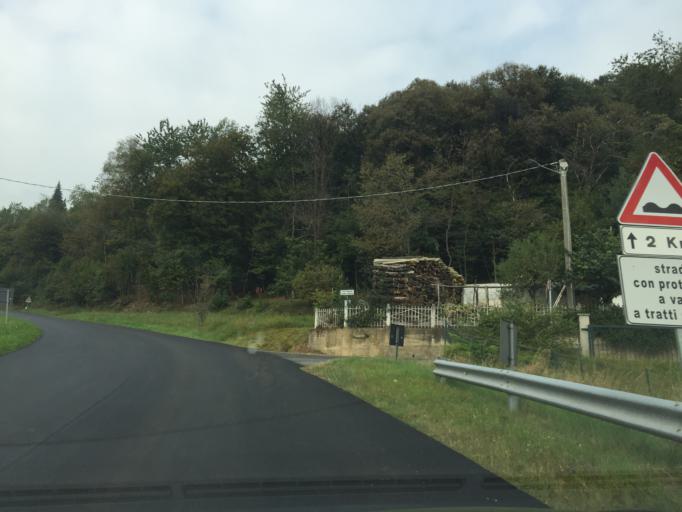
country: IT
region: Piedmont
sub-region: Provincia di Cuneo
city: Roccaforte Mondovi
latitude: 44.3107
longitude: 7.7155
